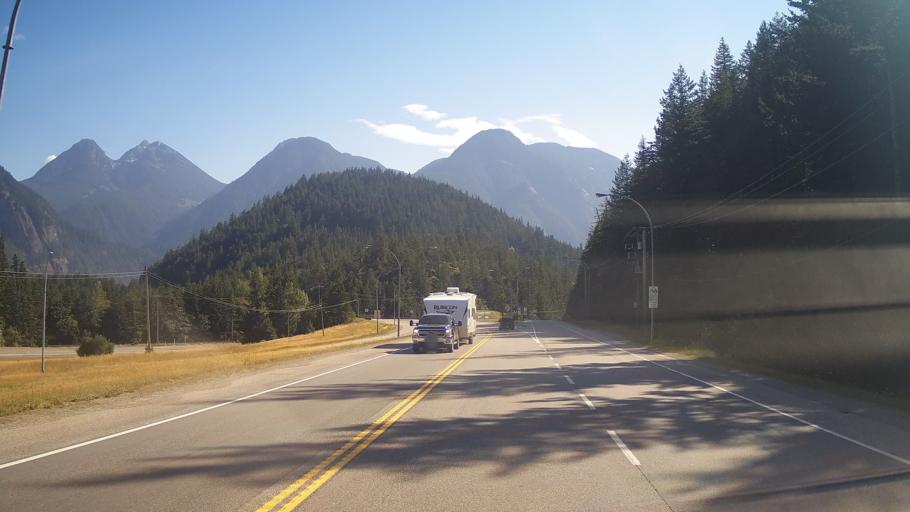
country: CA
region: British Columbia
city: Hope
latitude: 49.3933
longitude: -121.4594
